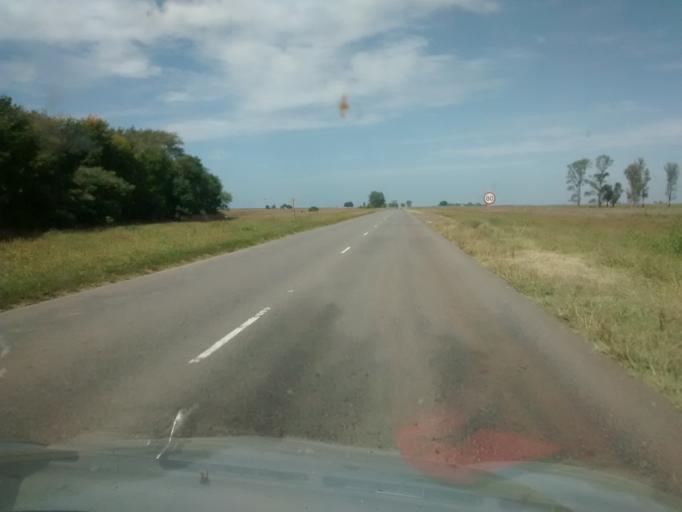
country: AR
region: Buenos Aires
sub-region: Partido de Ayacucho
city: Ayacucho
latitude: -37.2269
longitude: -58.4964
